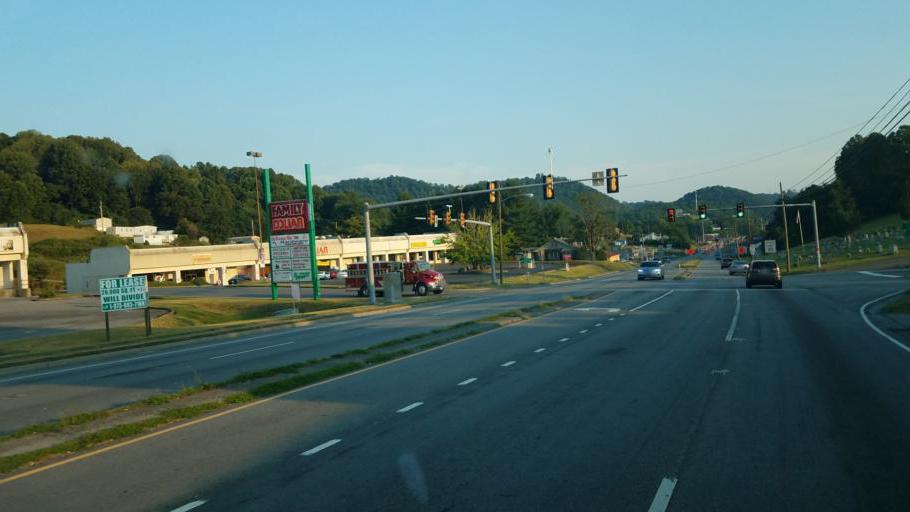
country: US
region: Virginia
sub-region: Scott County
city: Weber City
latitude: 36.6172
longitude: -82.5679
